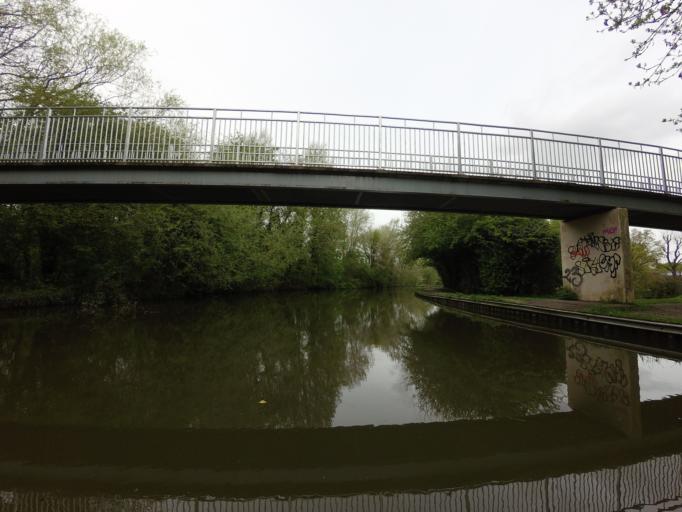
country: GB
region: England
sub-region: Milton Keynes
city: Simpson
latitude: 52.0230
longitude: -0.7234
